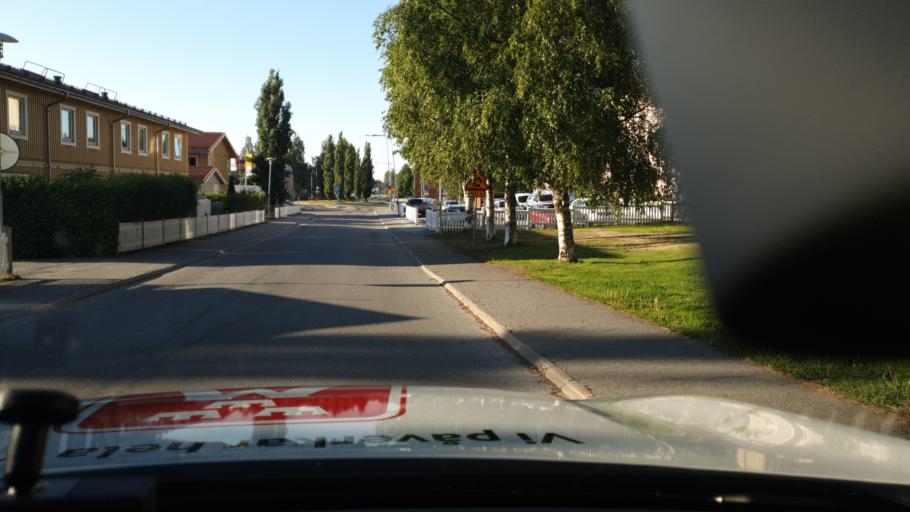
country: SE
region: Vaesterbotten
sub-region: Umea Kommun
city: Umea
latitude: 63.8193
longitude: 20.2389
